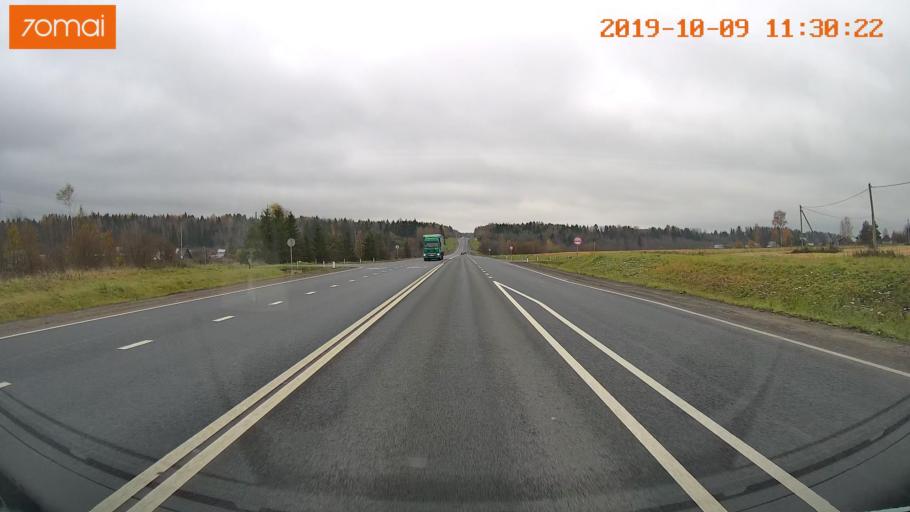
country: RU
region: Vologda
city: Gryazovets
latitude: 59.0544
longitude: 40.0736
